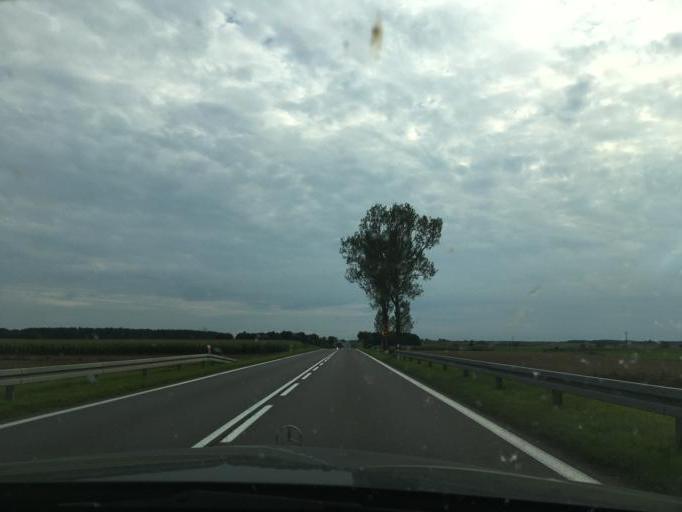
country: PL
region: Podlasie
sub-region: Powiat kolnenski
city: Stawiski
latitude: 53.4230
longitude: 22.1675
